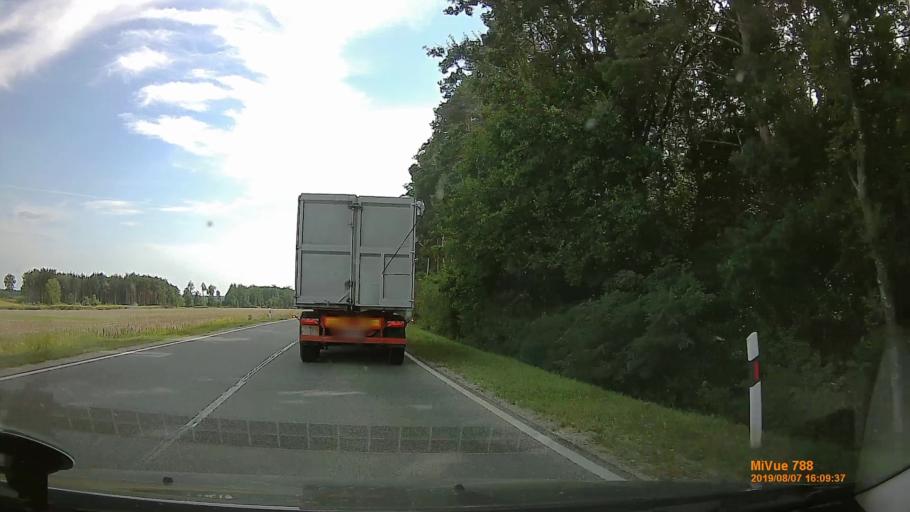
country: HU
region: Zala
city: Zalalovo
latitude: 46.8909
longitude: 16.6016
